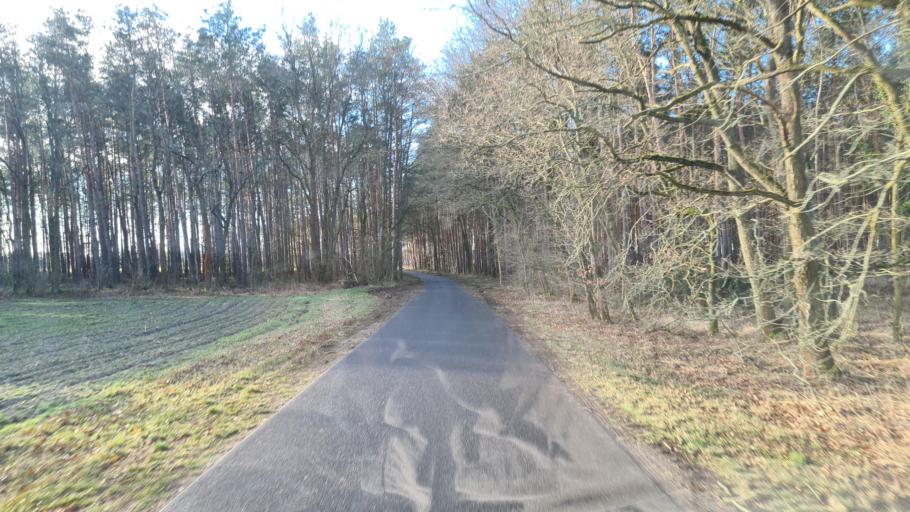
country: DE
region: Brandenburg
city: Herzberg
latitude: 51.6876
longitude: 13.2033
